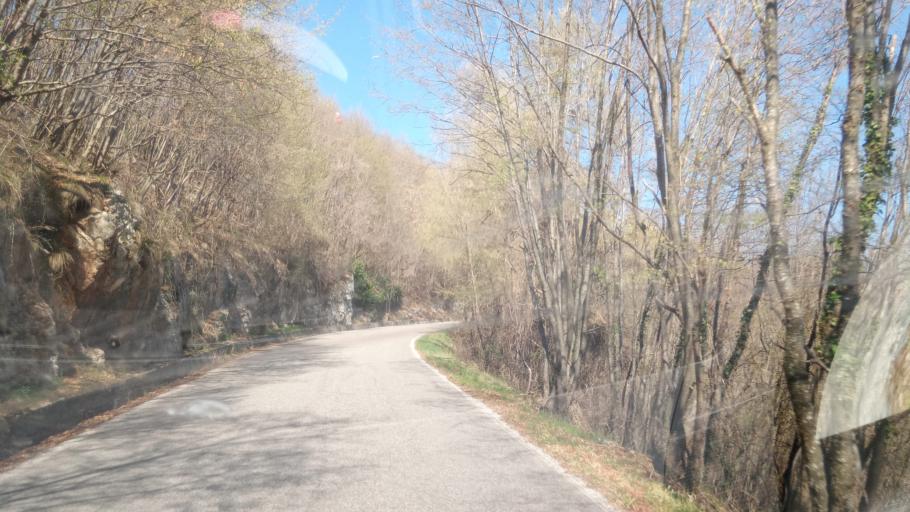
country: IT
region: Veneto
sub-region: Provincia di Treviso
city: Borso del Grappa
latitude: 45.8179
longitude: 11.7635
